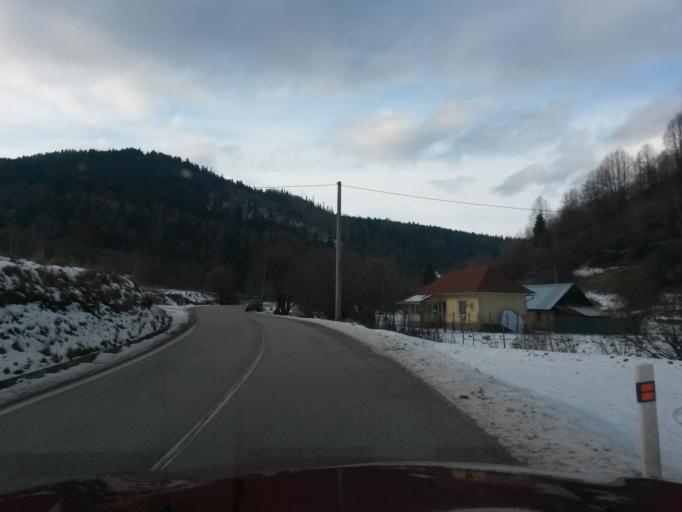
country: SK
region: Kosicky
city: Spisska Nova Ves
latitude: 48.8484
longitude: 20.5937
